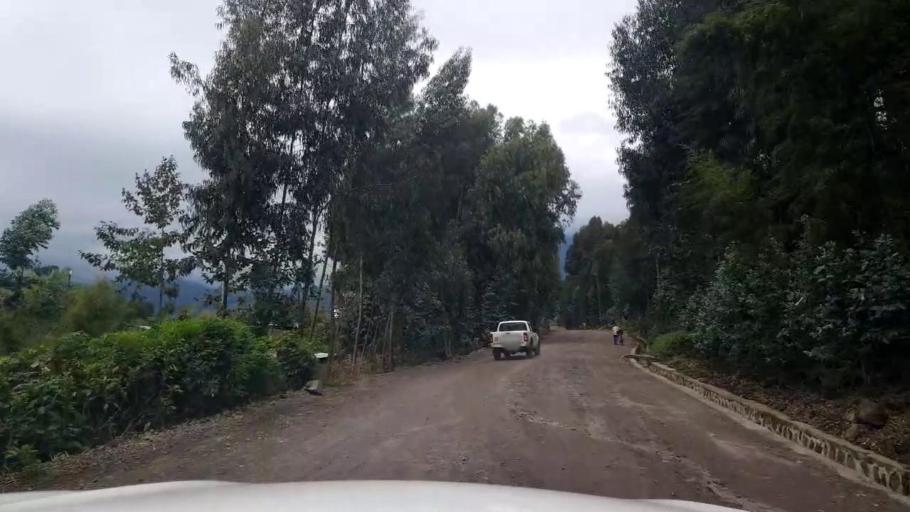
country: RW
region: Northern Province
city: Musanze
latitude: -1.4437
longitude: 29.5353
